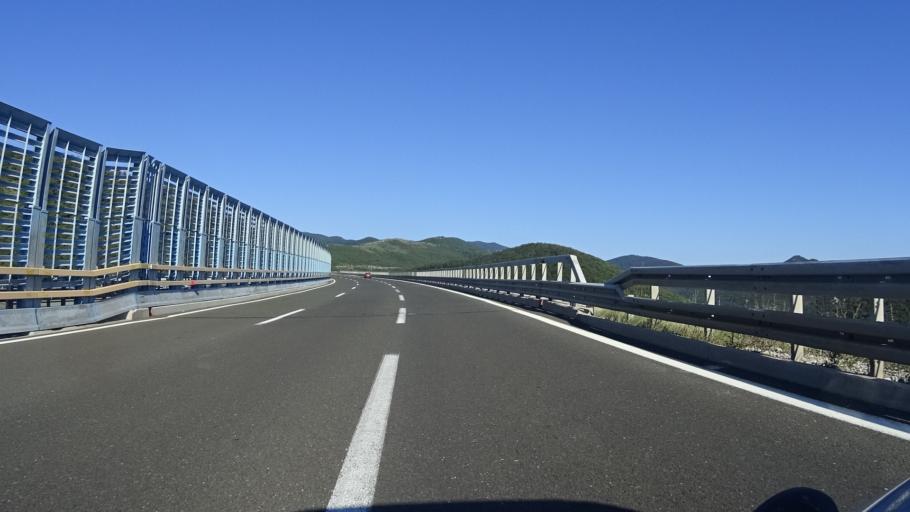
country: HR
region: Primorsko-Goranska
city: Skrljevo
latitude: 45.3618
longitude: 14.5558
